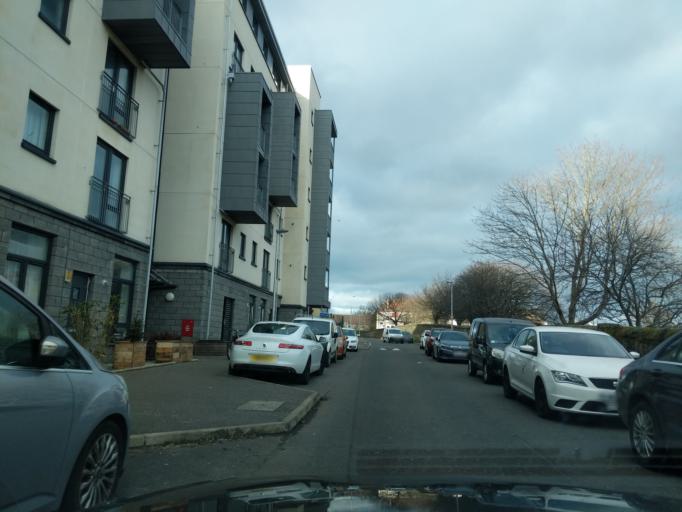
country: GB
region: Scotland
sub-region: West Lothian
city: Seafield
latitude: 55.9612
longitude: -3.1627
